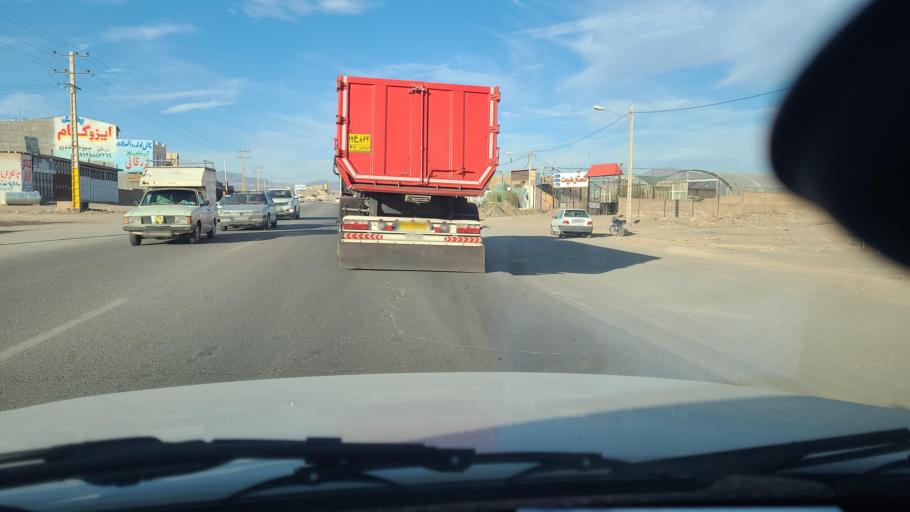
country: IR
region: Razavi Khorasan
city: Sabzevar
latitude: 36.2221
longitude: 57.6516
